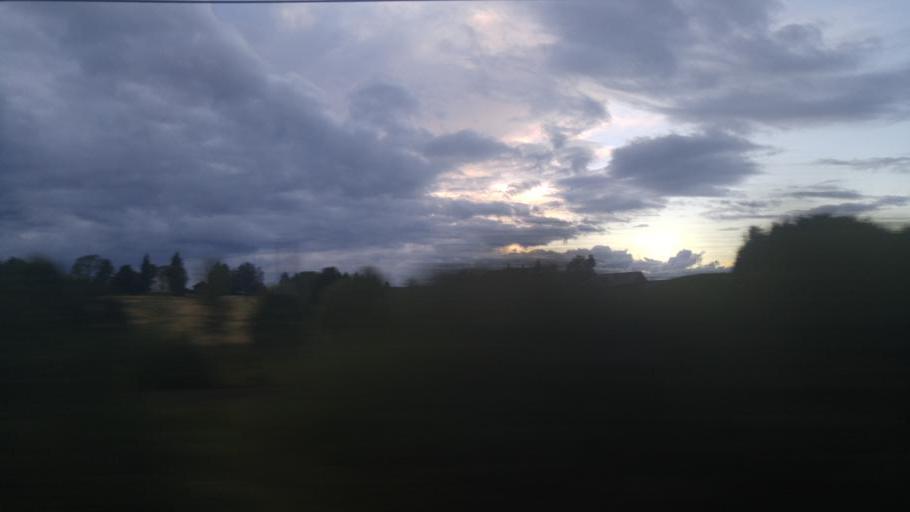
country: NO
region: Akershus
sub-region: Sorum
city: Frogner
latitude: 60.0103
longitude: 11.1036
